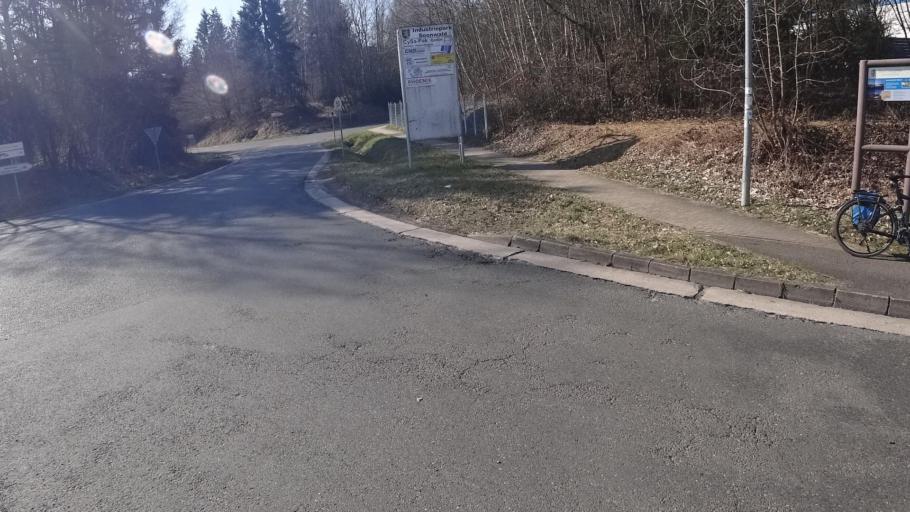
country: DE
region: Rheinland-Pfalz
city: Dichtelbach
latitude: 49.9936
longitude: 7.6863
